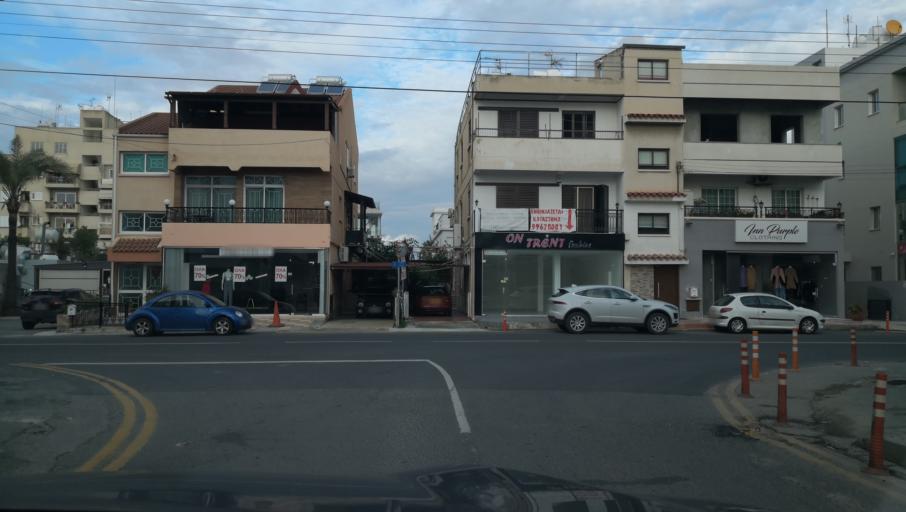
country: CY
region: Lefkosia
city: Nicosia
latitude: 35.1359
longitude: 33.3527
